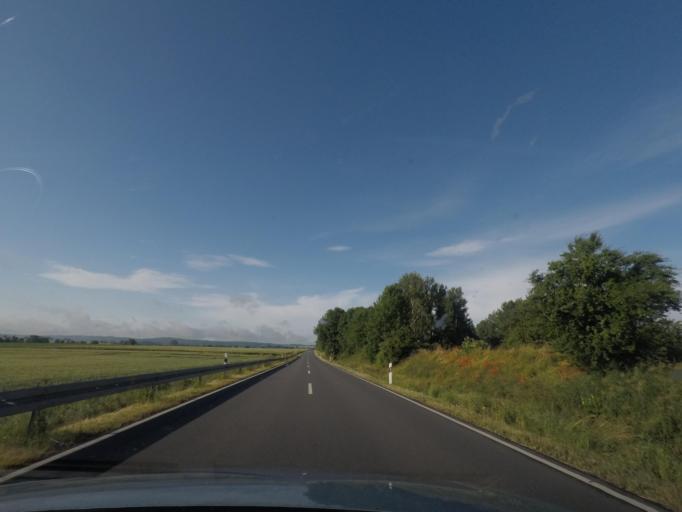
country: DE
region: Saxony-Anhalt
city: Huy-Neinstedt
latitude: 52.0039
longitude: 10.8950
